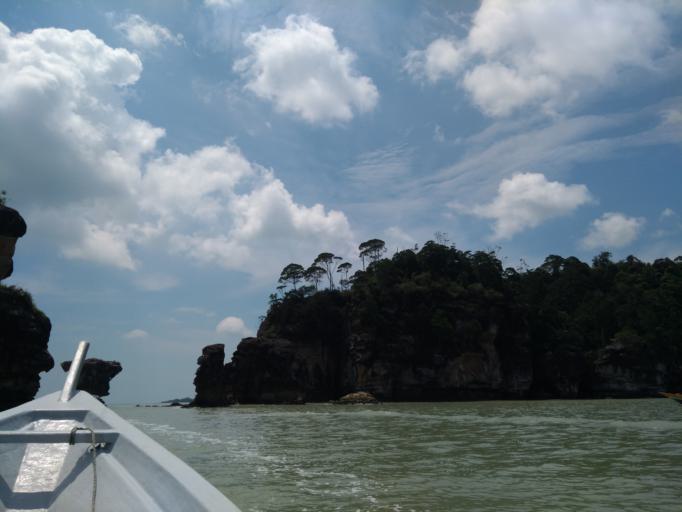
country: MY
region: Sarawak
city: Kuching
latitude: 1.7312
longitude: 110.4465
